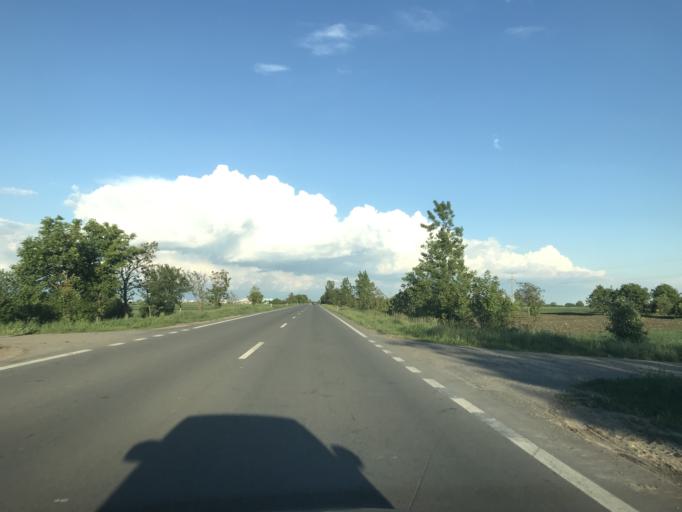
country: RS
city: Aradac
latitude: 45.3892
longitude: 20.3082
